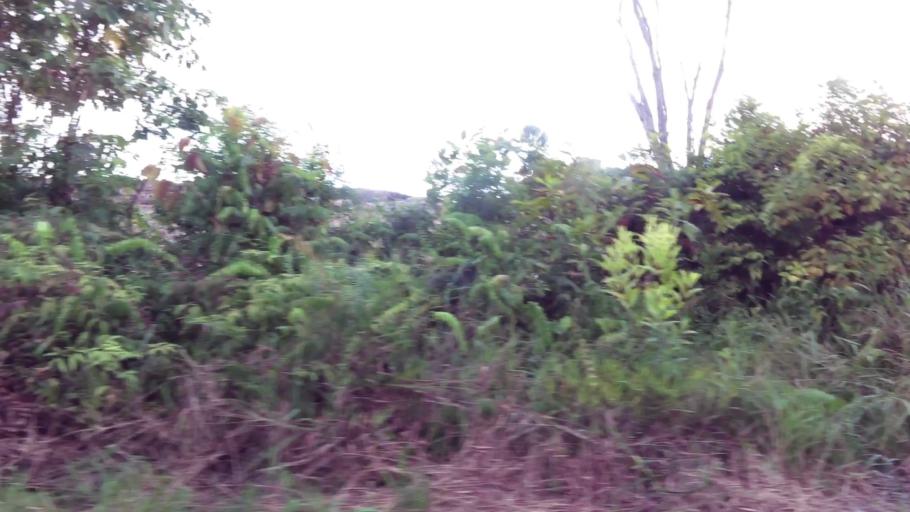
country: BN
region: Brunei and Muara
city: Bandar Seri Begawan
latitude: 4.9756
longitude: 114.9911
